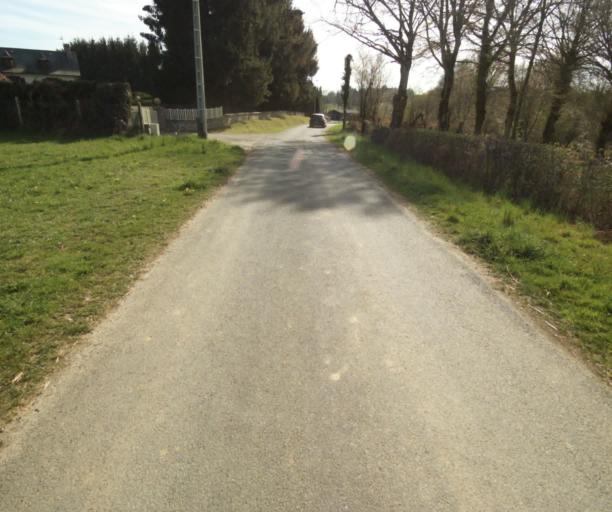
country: FR
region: Limousin
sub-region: Departement de la Correze
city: Naves
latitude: 45.3393
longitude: 1.7409
